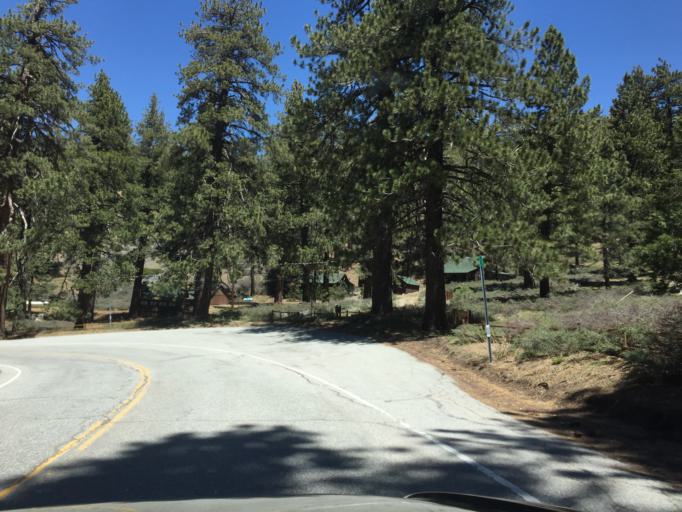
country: US
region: California
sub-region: San Bernardino County
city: Wrightwood
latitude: 34.3828
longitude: -117.6899
